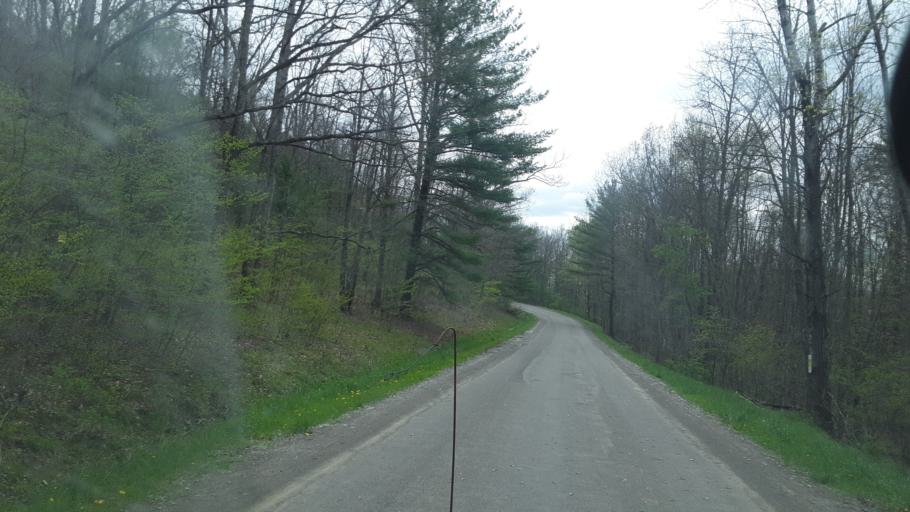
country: US
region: New York
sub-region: Steuben County
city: Addison
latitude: 42.0944
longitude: -77.3135
